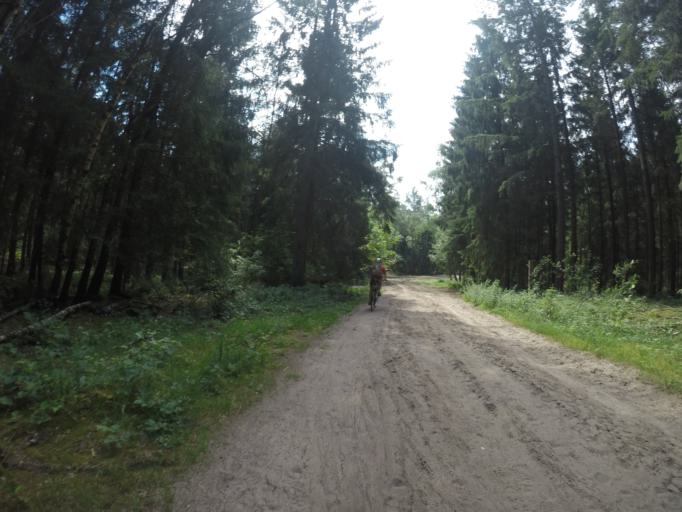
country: DE
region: Lower Saxony
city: Handeloh
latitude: 53.2886
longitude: 9.8449
